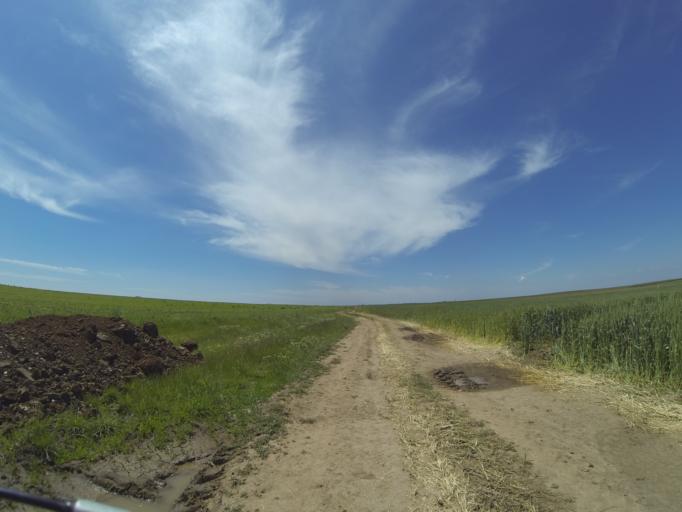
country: RO
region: Dolj
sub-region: Comuna Teslui
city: Teslui
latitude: 44.1902
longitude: 24.1569
